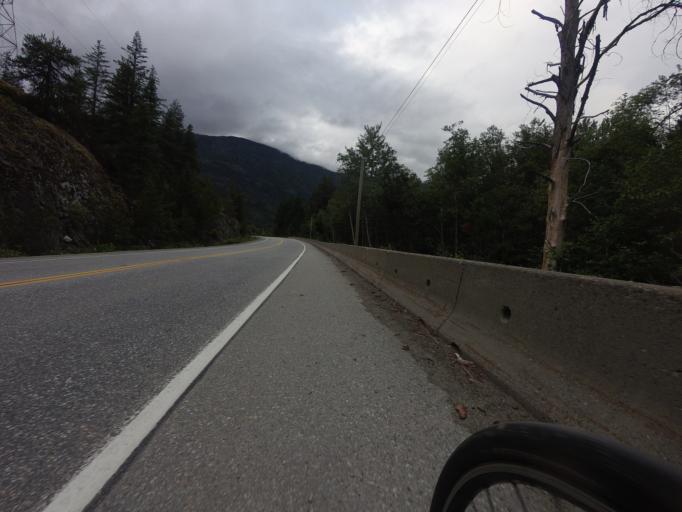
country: CA
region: British Columbia
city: Pemberton
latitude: 50.2624
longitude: -122.8651
